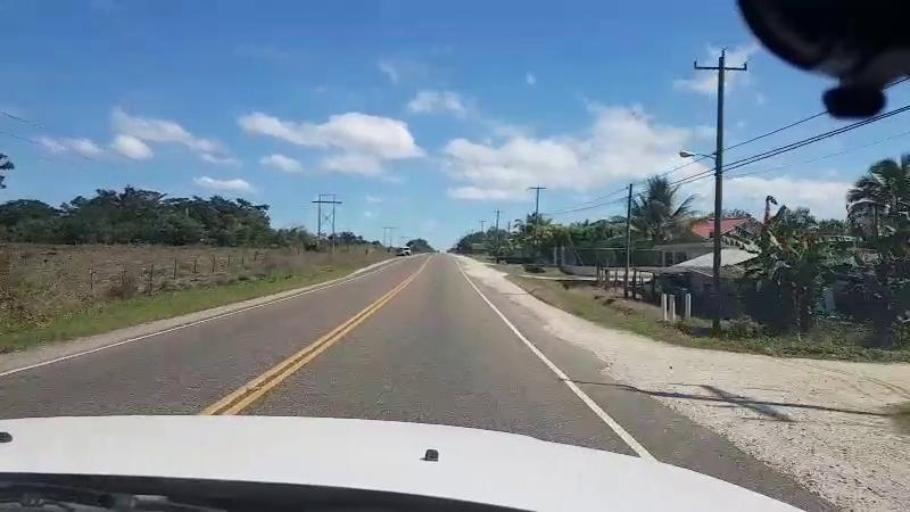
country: BZ
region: Cayo
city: Belmopan
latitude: 17.2768
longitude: -88.7206
